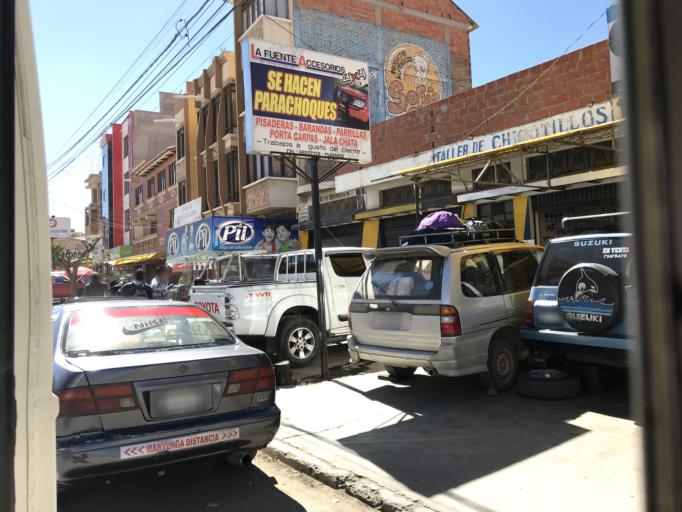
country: BO
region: Chuquisaca
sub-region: Provincia Oropeza
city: Huata
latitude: -19.0325
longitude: -65.2449
